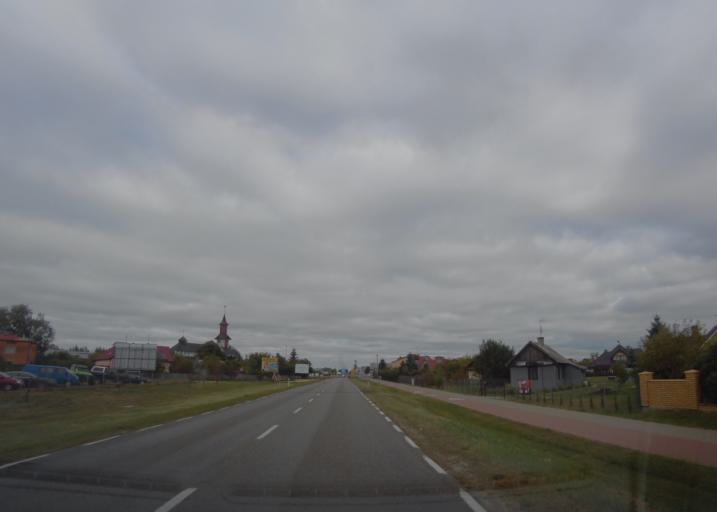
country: PL
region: Lublin Voivodeship
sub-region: Powiat wlodawski
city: Wlodawa
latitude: 51.5440
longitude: 23.5409
